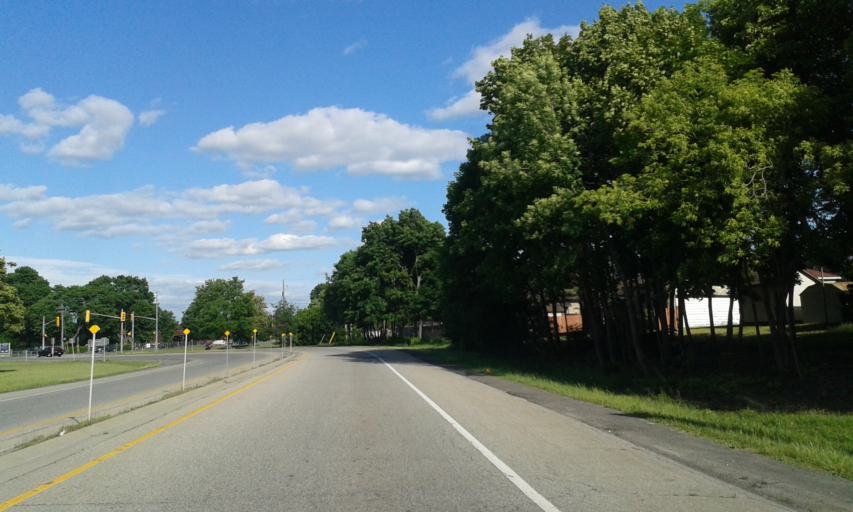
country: CA
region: Ontario
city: Prescott
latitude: 44.7212
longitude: -75.5256
